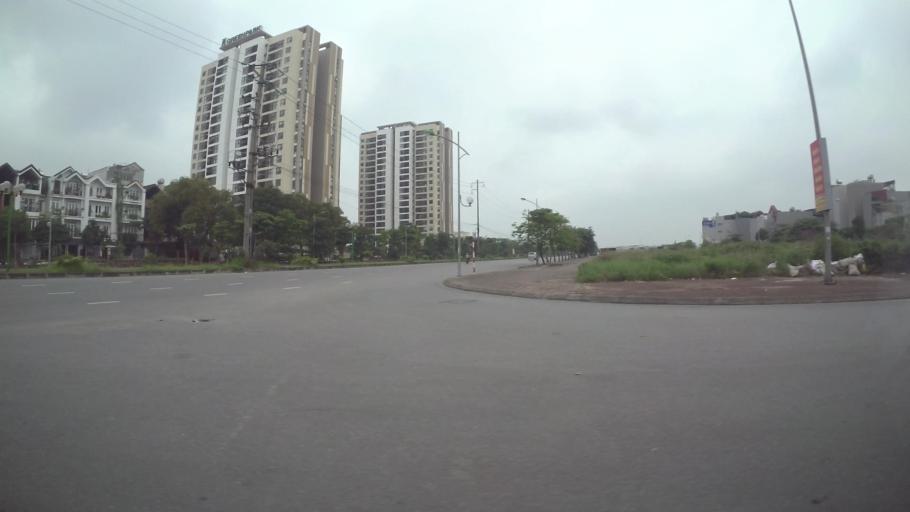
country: VN
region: Ha Noi
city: Trau Quy
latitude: 21.0632
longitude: 105.9128
